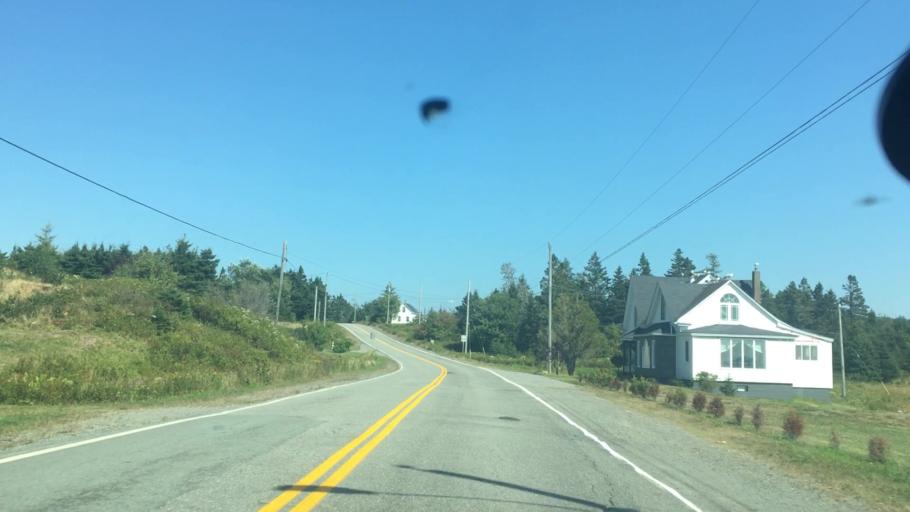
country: CA
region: Nova Scotia
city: New Glasgow
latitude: 44.9114
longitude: -62.3846
